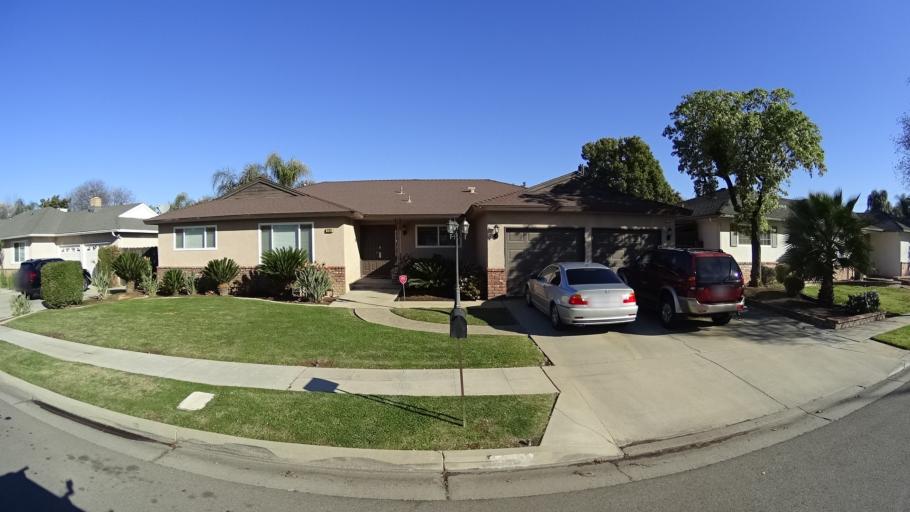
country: US
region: California
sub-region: Fresno County
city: Clovis
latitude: 36.8418
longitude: -119.7717
